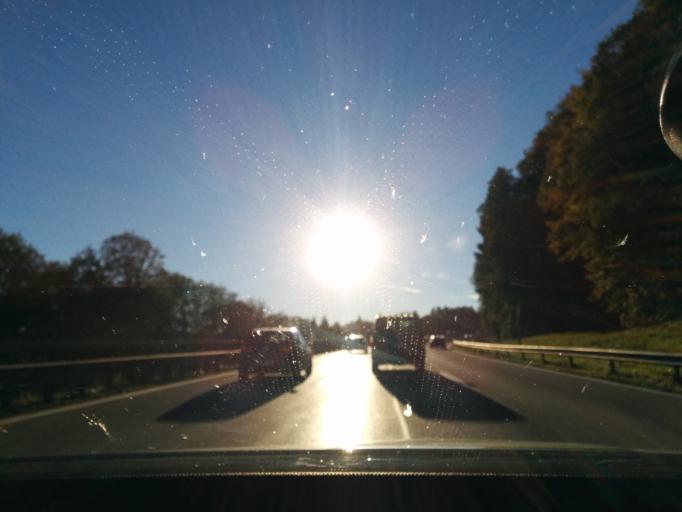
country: DE
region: Bavaria
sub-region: Upper Bavaria
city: Irschenberg
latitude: 47.8230
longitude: 11.9357
